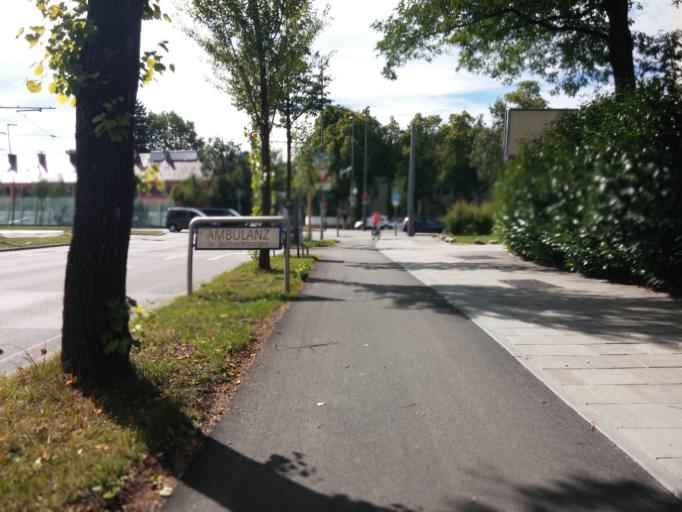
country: DE
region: Bavaria
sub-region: Upper Bavaria
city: Bogenhausen
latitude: 48.1540
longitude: 11.6166
